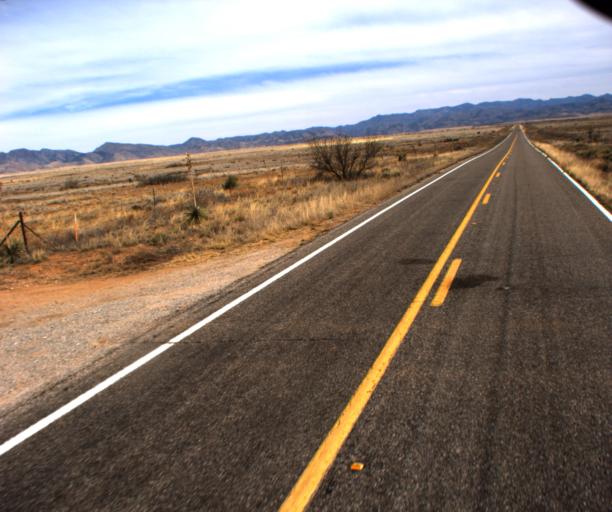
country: US
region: Arizona
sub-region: Cochise County
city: Willcox
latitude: 32.0744
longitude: -109.5153
